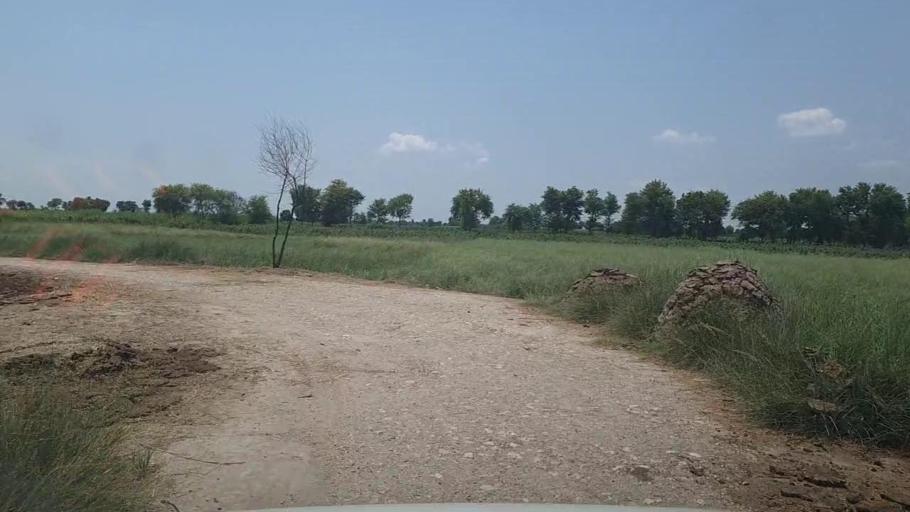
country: PK
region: Sindh
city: Ubauro
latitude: 28.1556
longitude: 69.7497
